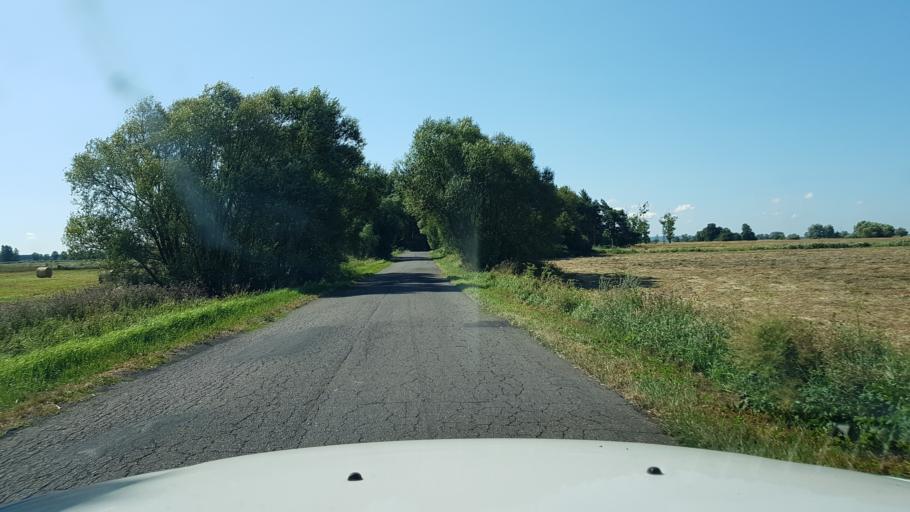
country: PL
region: West Pomeranian Voivodeship
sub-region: Powiat goleniowski
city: Goleniow
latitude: 53.4857
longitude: 14.7117
